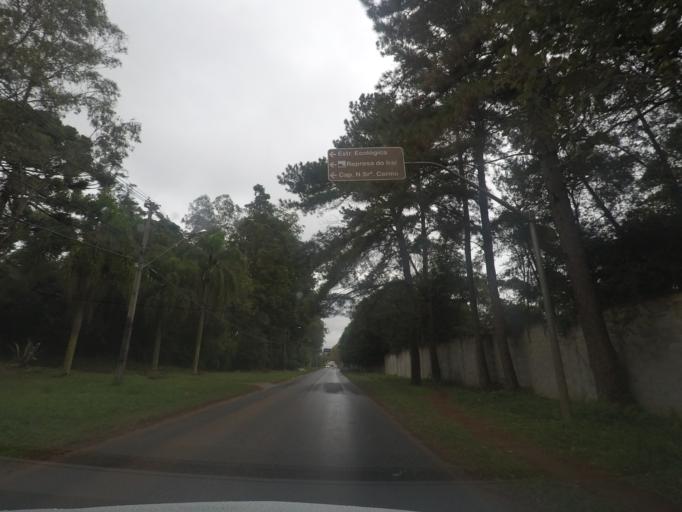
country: BR
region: Parana
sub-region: Pinhais
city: Pinhais
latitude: -25.3902
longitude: -49.1523
